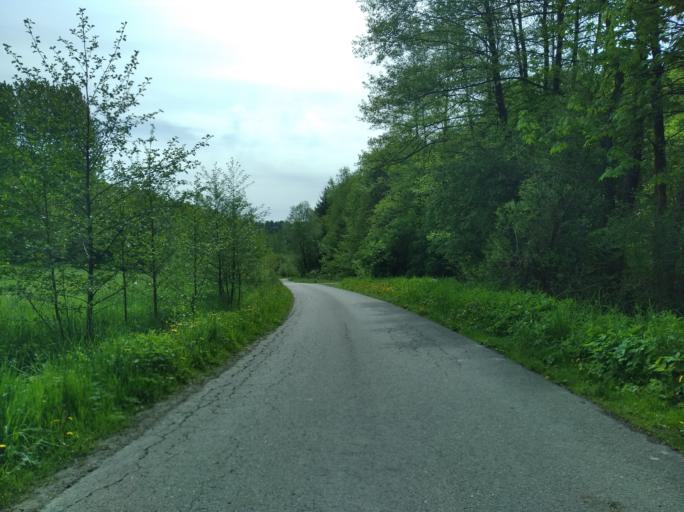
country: PL
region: Subcarpathian Voivodeship
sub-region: Powiat strzyzowski
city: Strzyzow
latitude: 49.9275
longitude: 21.7459
